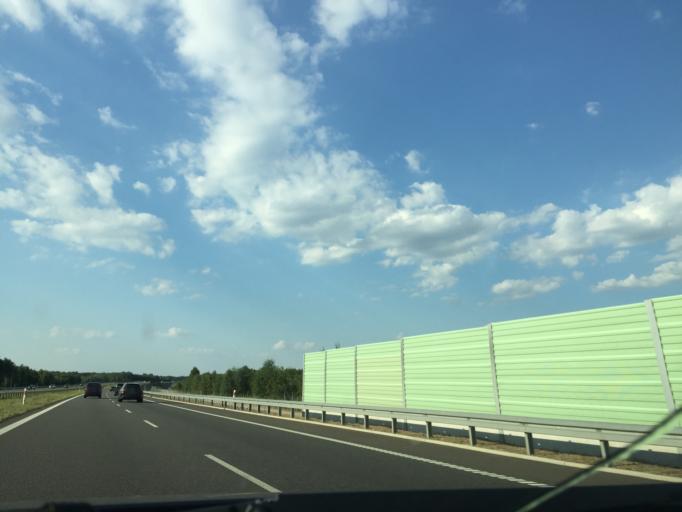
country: PL
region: Masovian Voivodeship
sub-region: Powiat radomski
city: Wolanow
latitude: 51.3578
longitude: 21.0147
